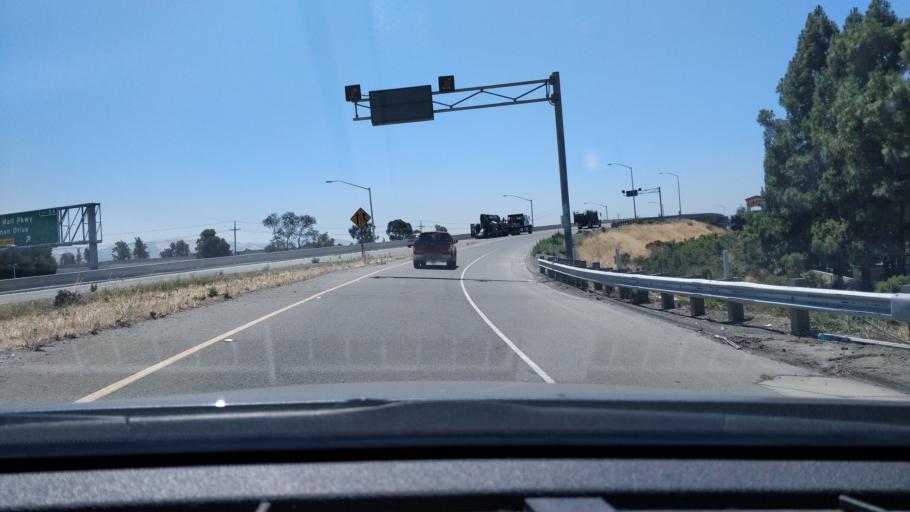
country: US
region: California
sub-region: Santa Clara County
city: Milpitas
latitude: 37.4237
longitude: -121.9166
